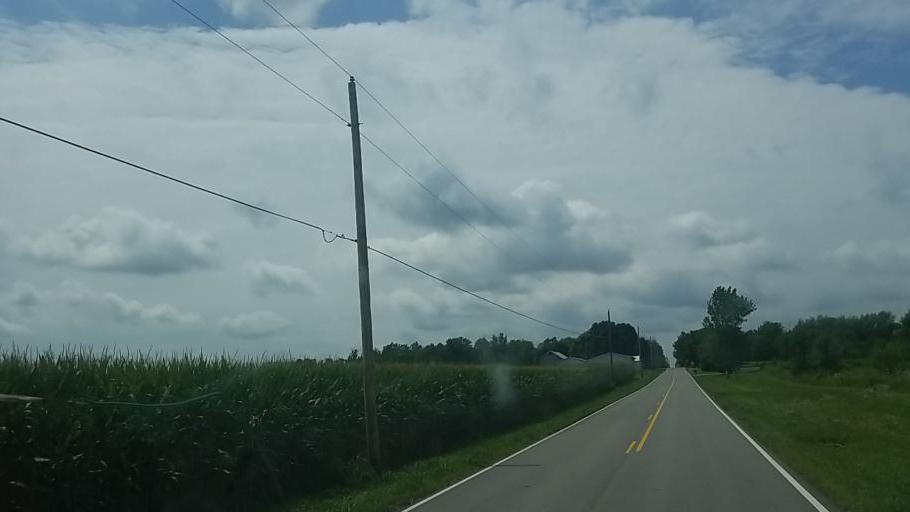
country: US
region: Ohio
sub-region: Fairfield County
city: Lithopolis
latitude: 39.7496
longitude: -82.7953
